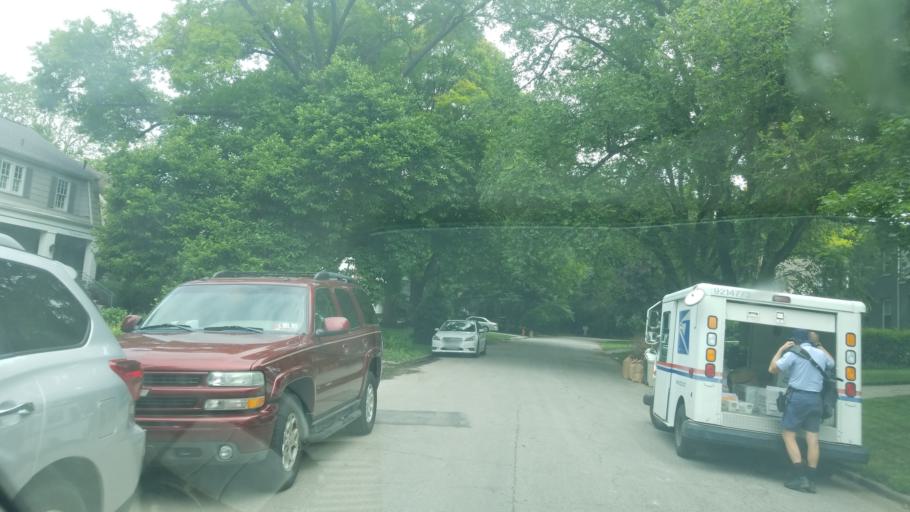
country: US
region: Ohio
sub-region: Franklin County
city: Upper Arlington
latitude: 40.0366
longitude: -83.0256
